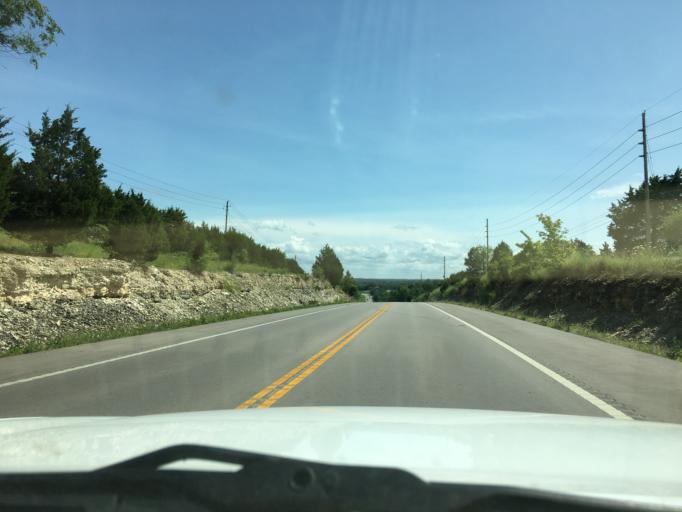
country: US
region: Missouri
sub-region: Franklin County
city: Union
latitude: 38.4724
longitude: -91.0058
